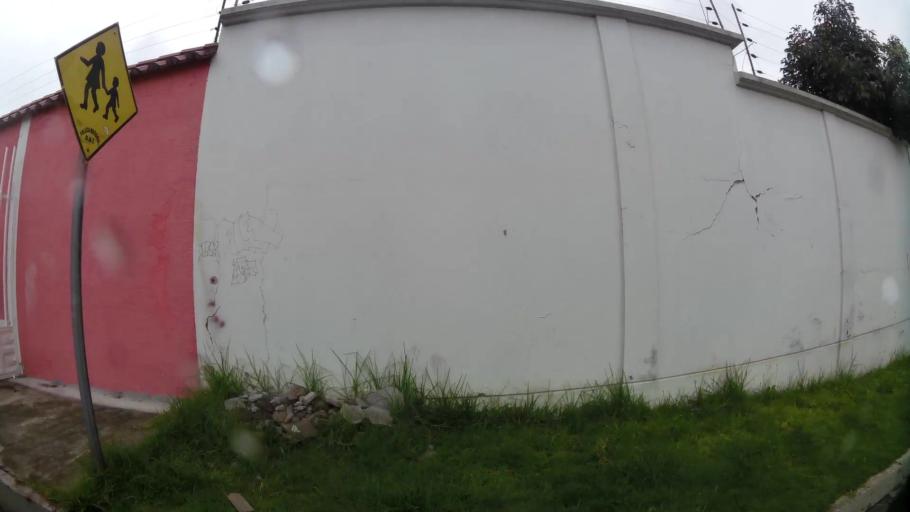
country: EC
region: Pichincha
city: Sangolqui
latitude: -0.2827
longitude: -78.4668
